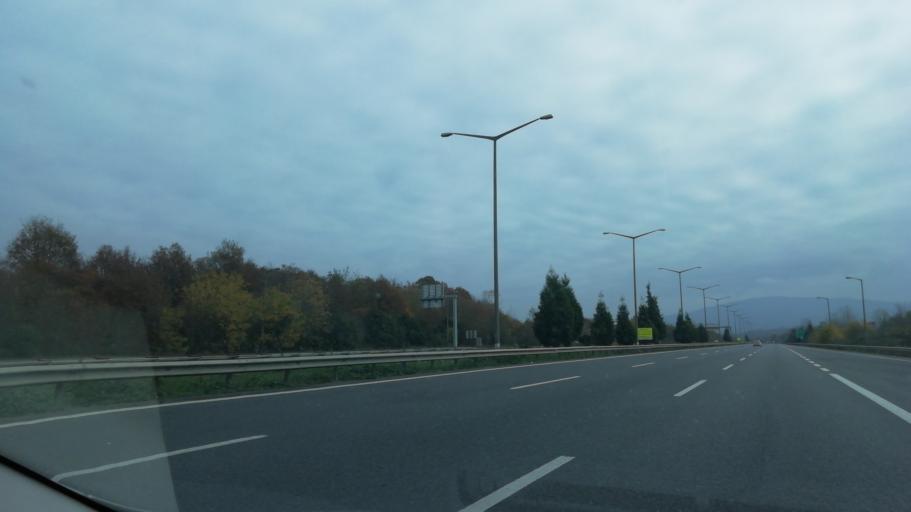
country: TR
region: Sakarya
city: Hendek
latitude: 40.7537
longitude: 30.7210
